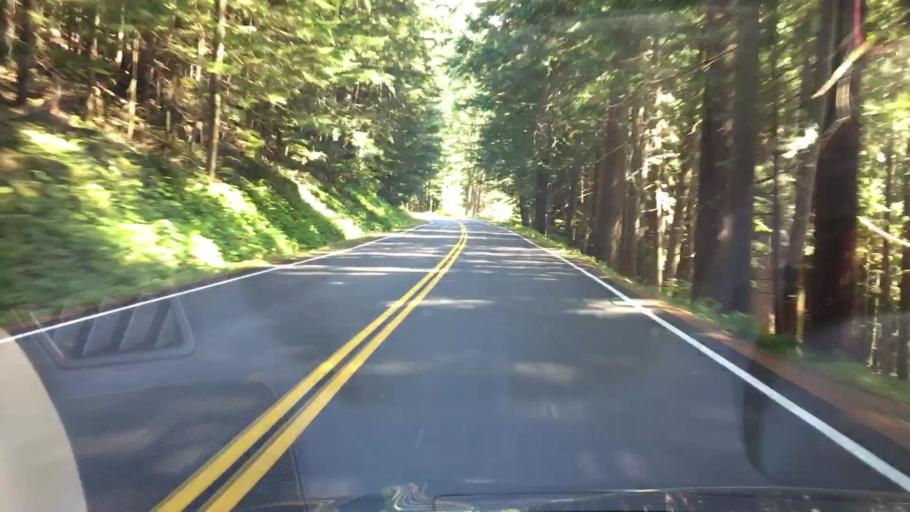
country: US
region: Washington
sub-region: Pierce County
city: Eatonville
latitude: 46.7350
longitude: -121.8750
